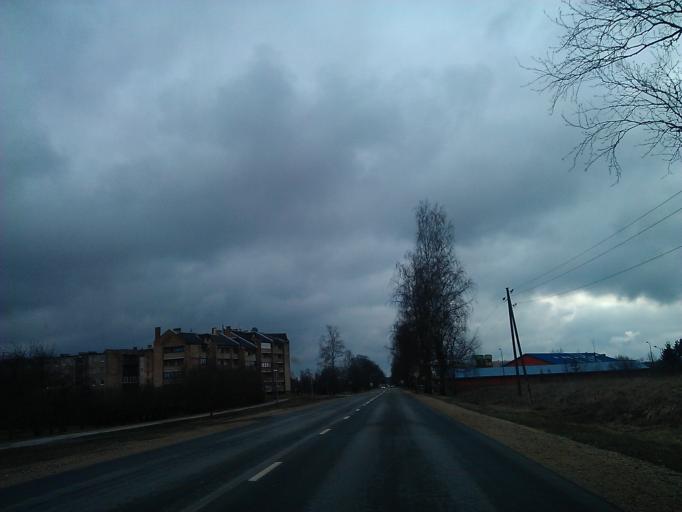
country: LV
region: Adazi
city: Adazi
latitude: 57.0829
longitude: 24.3171
